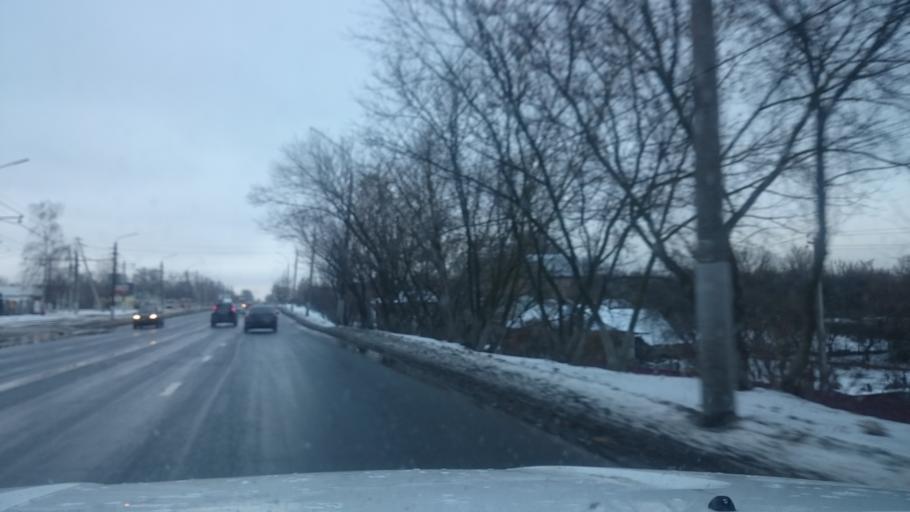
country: RU
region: Tula
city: Mendeleyevskiy
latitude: 54.1419
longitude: 37.5812
